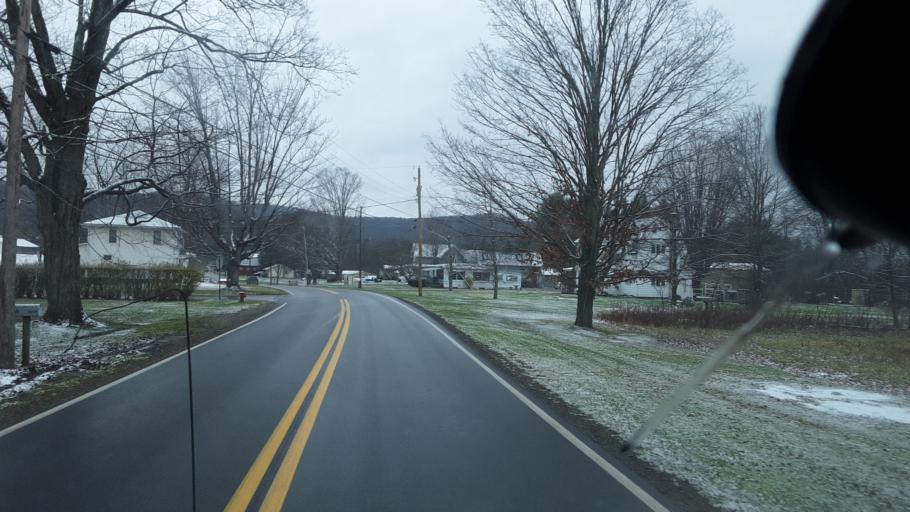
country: US
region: Pennsylvania
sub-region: Potter County
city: Shinglehouse
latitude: 41.9662
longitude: -78.1899
